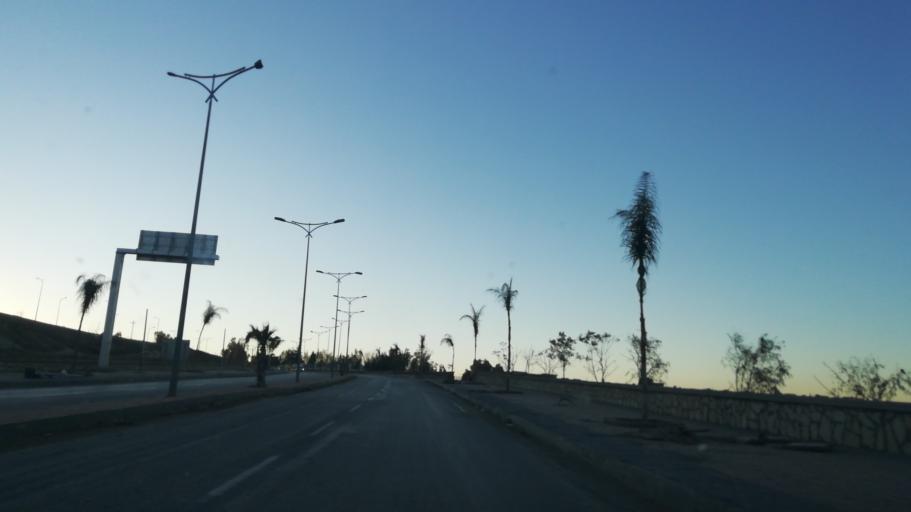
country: DZ
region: Saida
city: Saida
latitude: 34.8349
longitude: 0.1745
